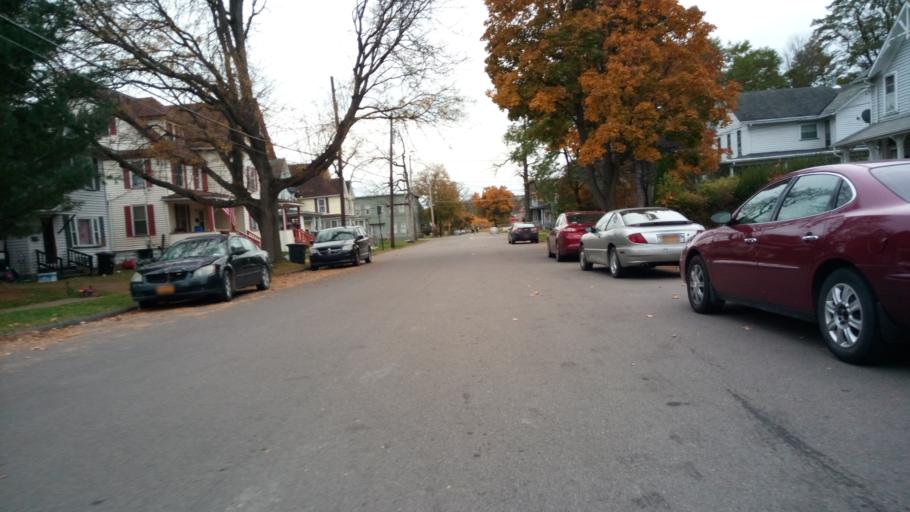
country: US
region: New York
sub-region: Chemung County
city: Elmira
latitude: 42.0835
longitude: -76.7967
